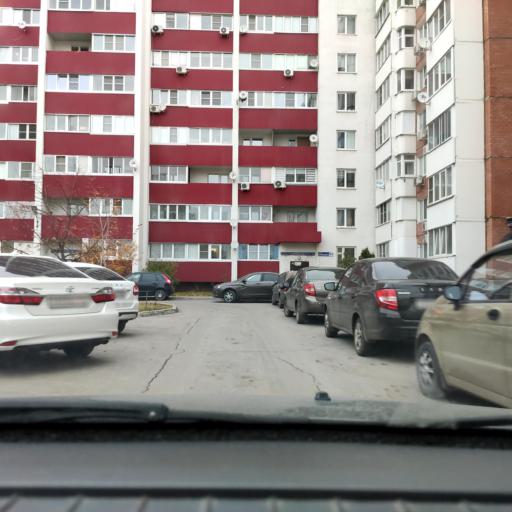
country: RU
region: Samara
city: Tol'yatti
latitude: 53.5420
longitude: 49.4027
